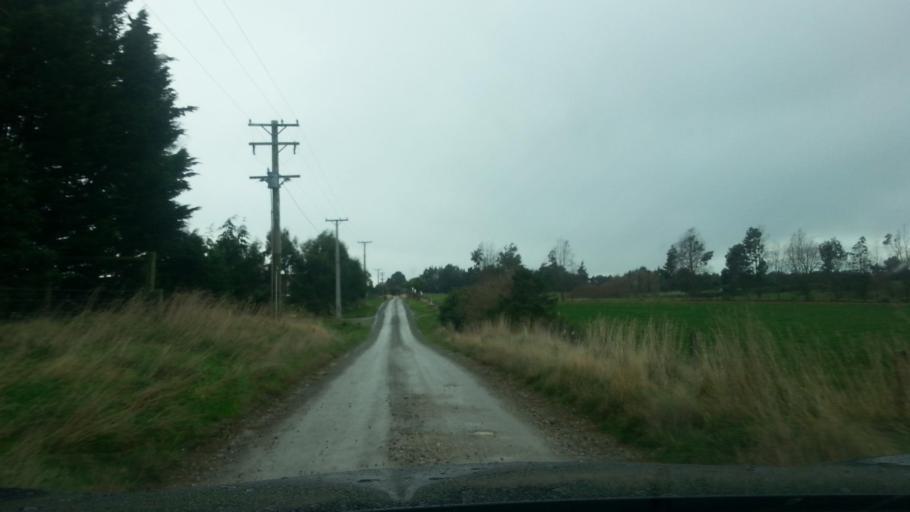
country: NZ
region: Southland
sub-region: Invercargill City
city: Invercargill
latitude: -46.3386
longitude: 168.4092
